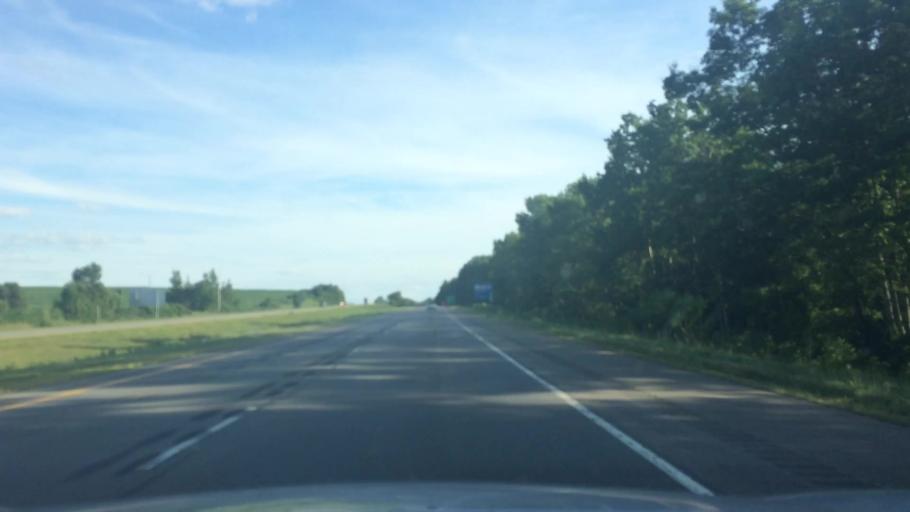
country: US
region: Wisconsin
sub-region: Marathon County
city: Mosinee
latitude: 44.7956
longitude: -89.6797
